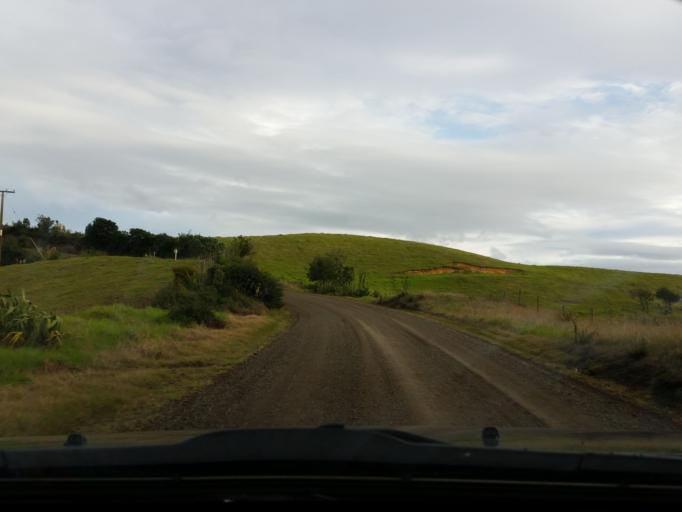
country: NZ
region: Northland
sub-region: Kaipara District
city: Dargaville
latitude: -35.8437
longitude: 173.6609
